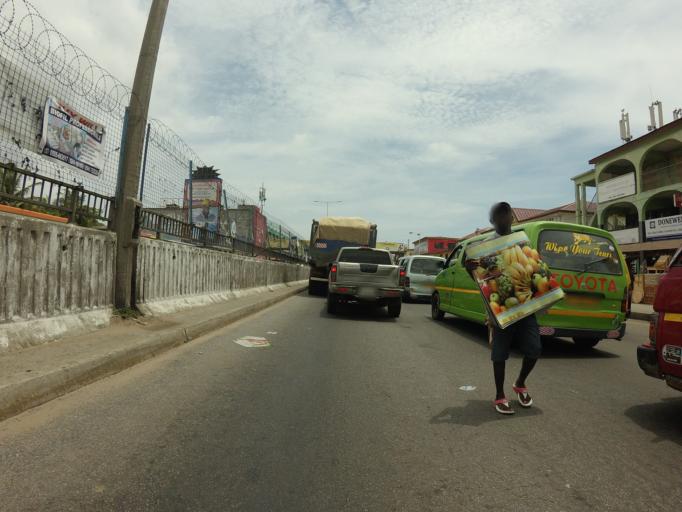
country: GH
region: Greater Accra
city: Accra
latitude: 5.5667
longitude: -0.2383
